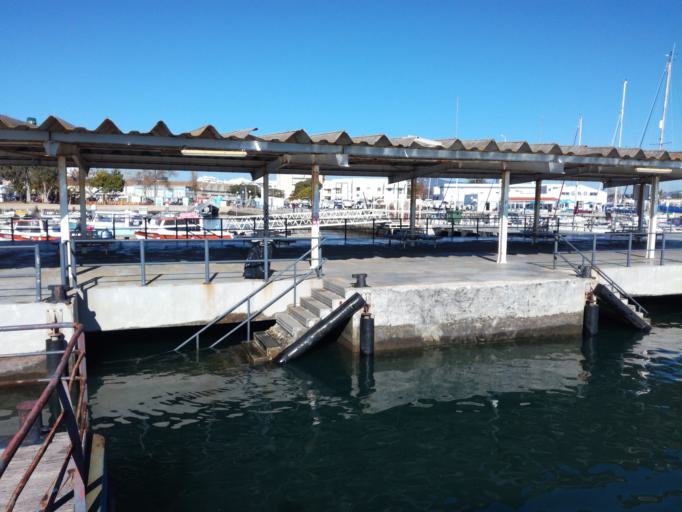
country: PT
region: Faro
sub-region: Olhao
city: Olhao
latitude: 37.0225
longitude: -7.8372
